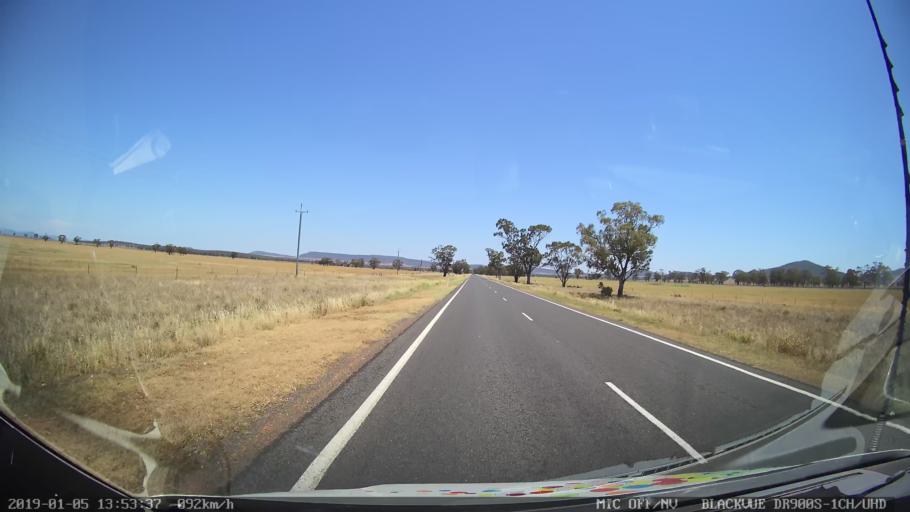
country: AU
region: New South Wales
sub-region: Gunnedah
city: Gunnedah
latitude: -31.0774
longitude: 150.2768
